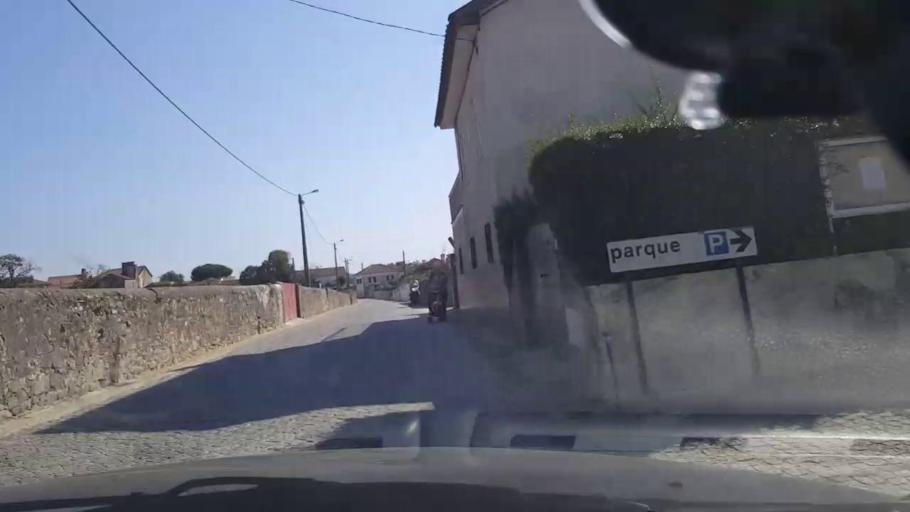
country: PT
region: Porto
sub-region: Povoa de Varzim
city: Pedroso
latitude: 41.4027
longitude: -8.6867
